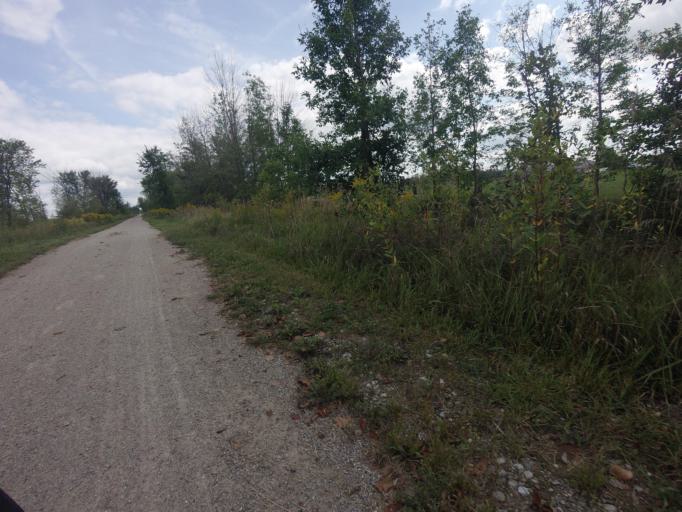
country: CA
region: Ontario
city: North Perth
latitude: 43.5717
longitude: -80.8695
